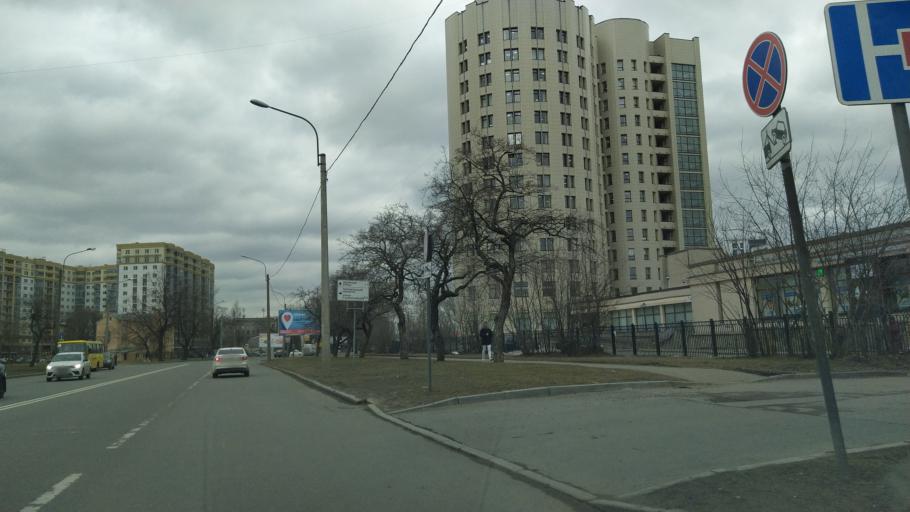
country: RU
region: St.-Petersburg
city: Centralniy
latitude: 59.9317
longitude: 30.4162
